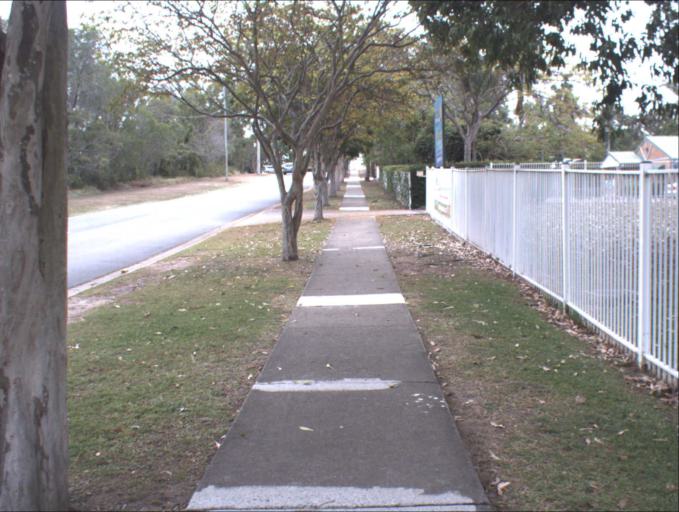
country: AU
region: Queensland
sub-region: Gold Coast
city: Yatala
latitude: -27.6796
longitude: 153.2360
